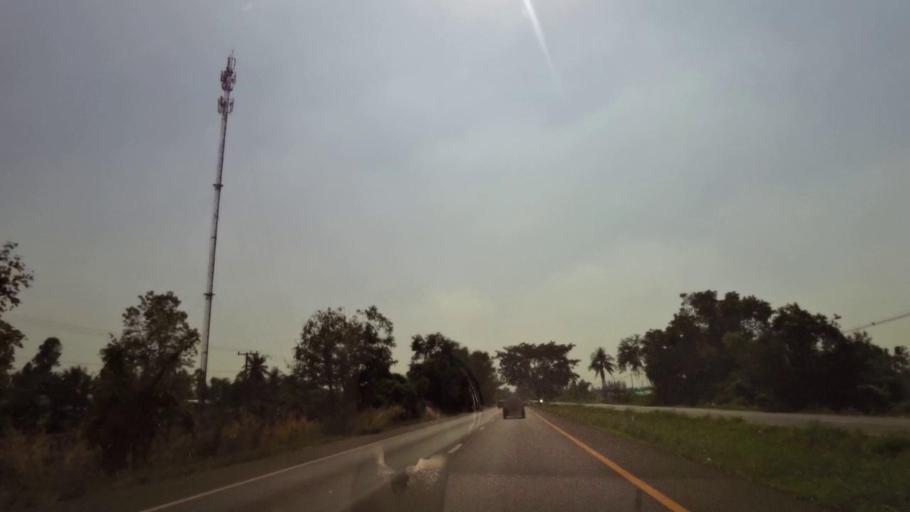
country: TH
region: Phichit
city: Bueng Na Rang
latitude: 16.0400
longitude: 100.1177
